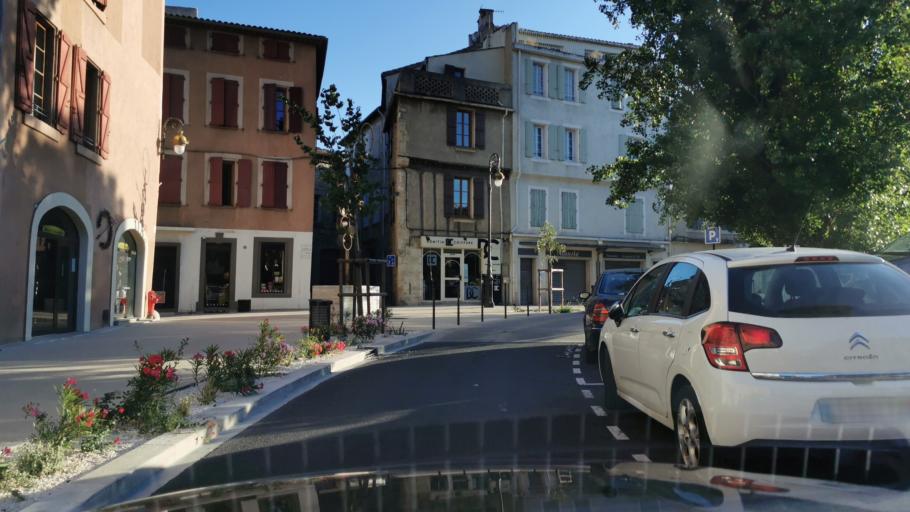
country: FR
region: Languedoc-Roussillon
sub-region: Departement de l'Aude
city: Narbonne
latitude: 43.1828
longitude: 3.0024
